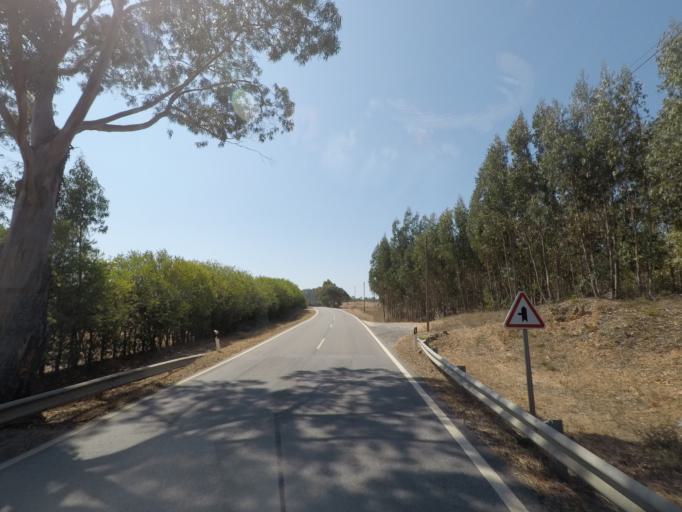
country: PT
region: Beja
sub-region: Odemira
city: Sao Teotonio
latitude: 37.5379
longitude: -8.6911
